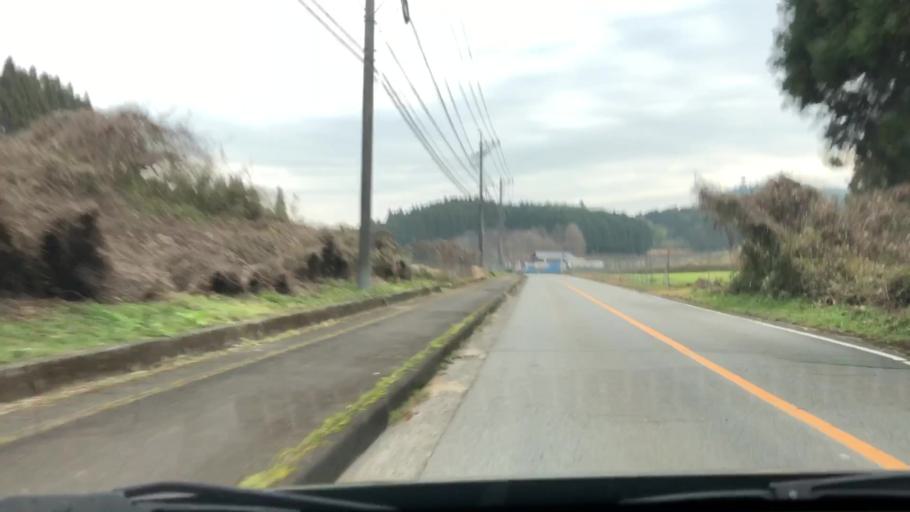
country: JP
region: Oita
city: Usuki
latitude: 33.0048
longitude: 131.6528
